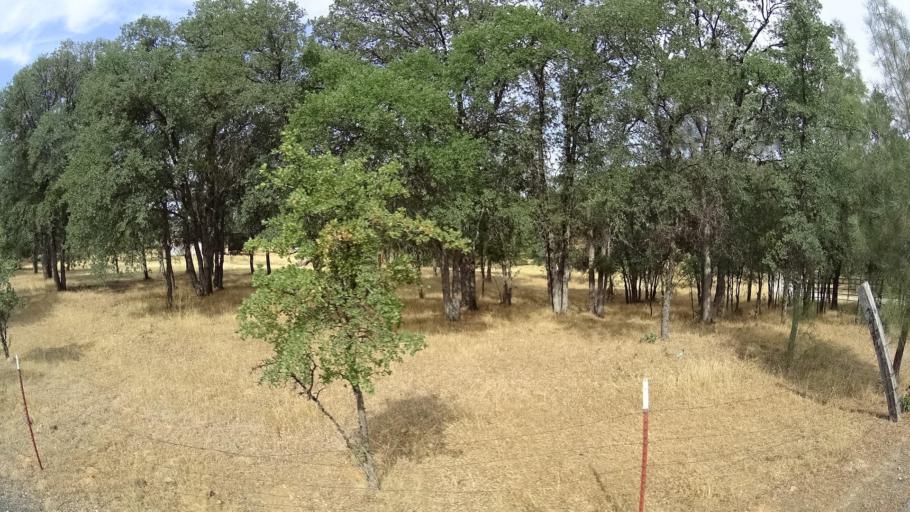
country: US
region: California
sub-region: Mariposa County
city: Midpines
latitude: 37.5446
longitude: -119.9683
